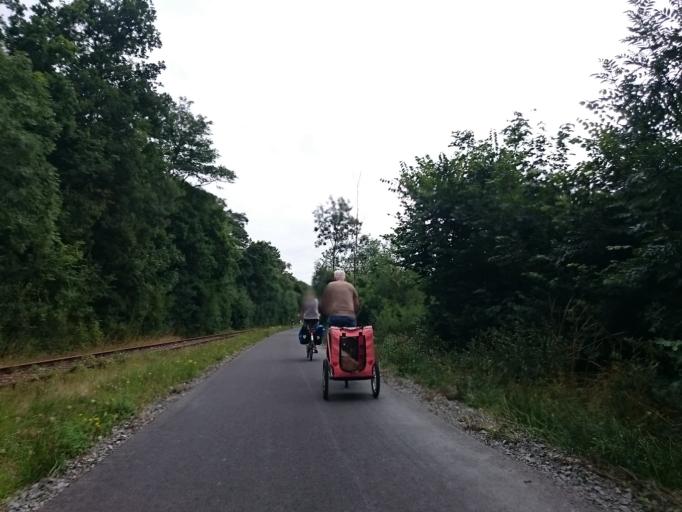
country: FR
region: Lower Normandy
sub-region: Departement du Calvados
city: Clinchamps-sur-Orne
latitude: 49.0732
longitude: -0.4306
